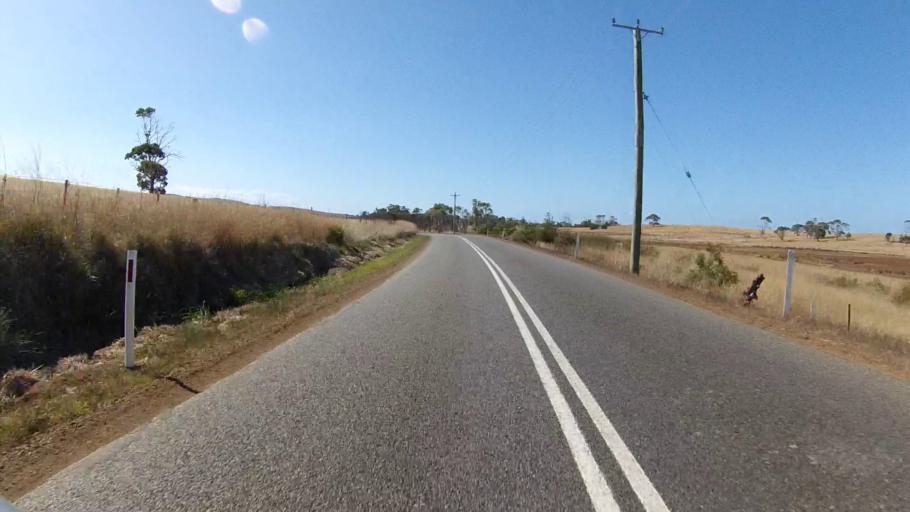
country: AU
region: Tasmania
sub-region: Sorell
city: Sorell
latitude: -42.2775
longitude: 148.0036
